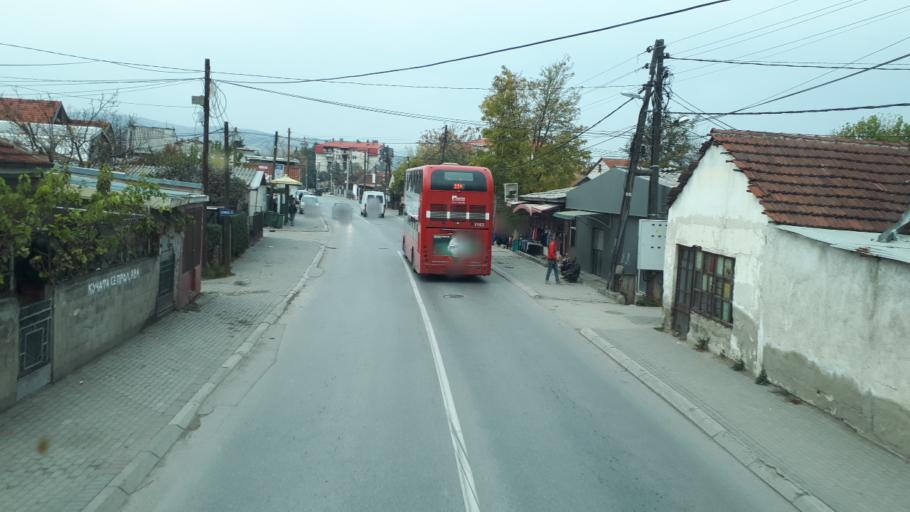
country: MK
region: Saraj
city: Saraj
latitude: 42.0156
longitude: 21.3580
